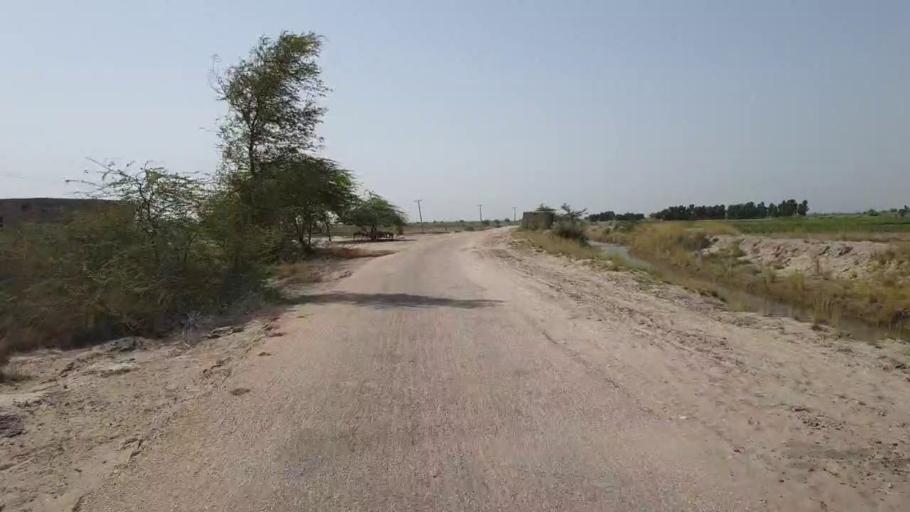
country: PK
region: Sindh
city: Jam Sahib
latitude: 26.4167
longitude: 68.9089
